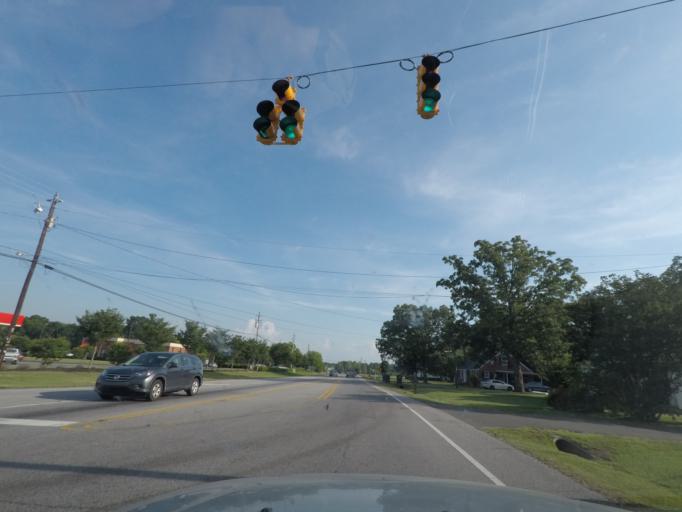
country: US
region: North Carolina
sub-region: Granville County
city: Oxford
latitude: 36.2810
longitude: -78.6068
